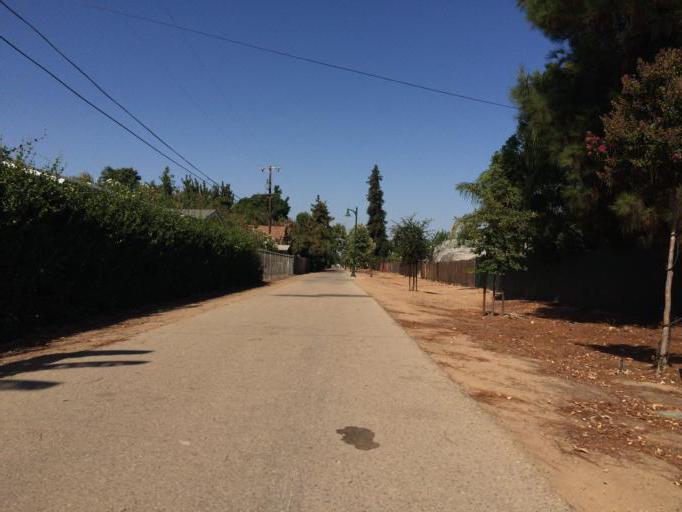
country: US
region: California
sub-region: Fresno County
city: Sunnyside
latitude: 36.7468
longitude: -119.7094
